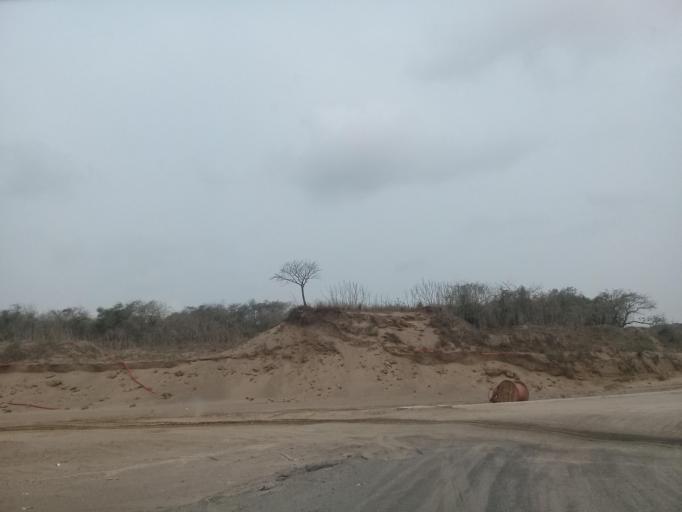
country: MX
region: Veracruz
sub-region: Veracruz
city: Rio Medio [Granja]
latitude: 19.2243
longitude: -96.2002
